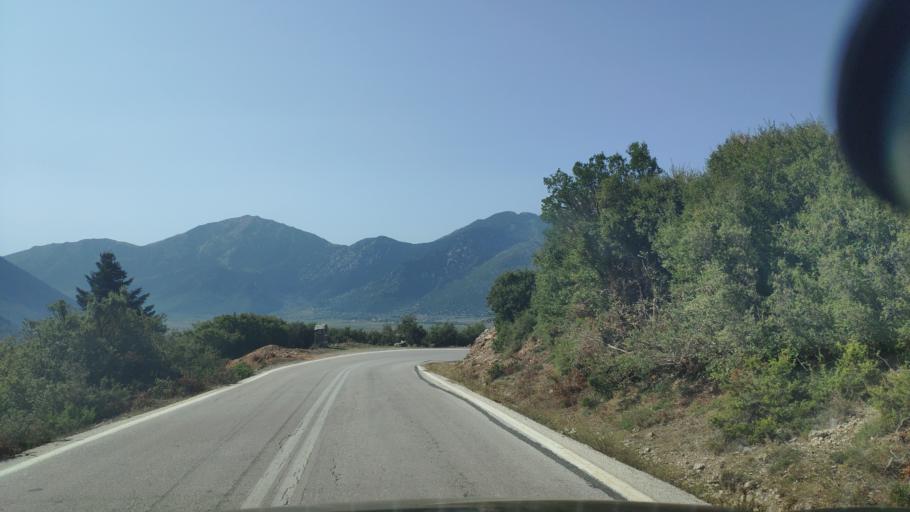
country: GR
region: West Greece
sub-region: Nomos Achaias
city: Aiyira
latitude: 37.8791
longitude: 22.3542
